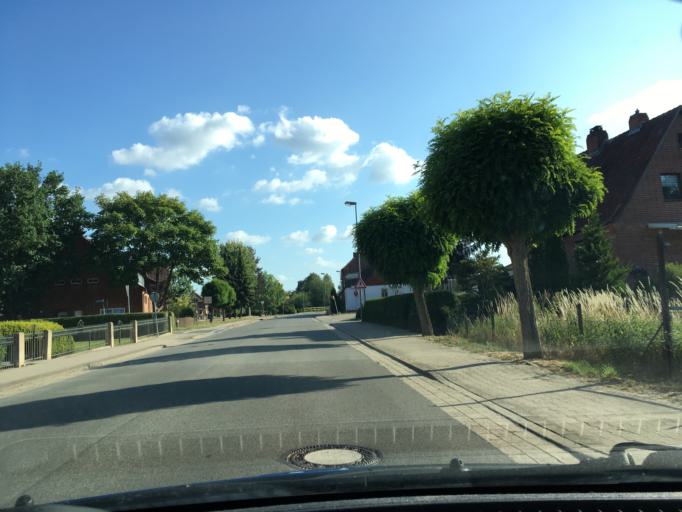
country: DE
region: Lower Saxony
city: Dahlenburg
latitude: 53.1866
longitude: 10.7358
